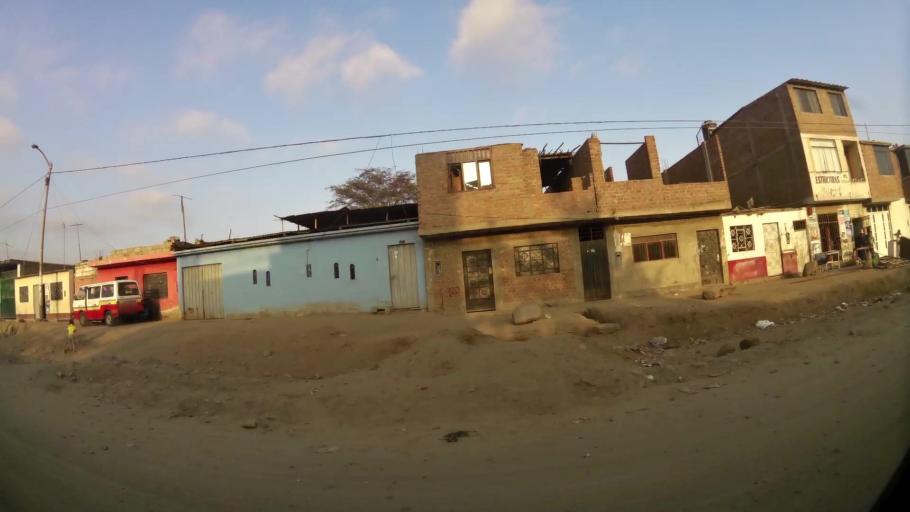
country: PE
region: La Libertad
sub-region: Provincia de Trujillo
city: El Porvenir
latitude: -8.0701
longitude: -78.9971
